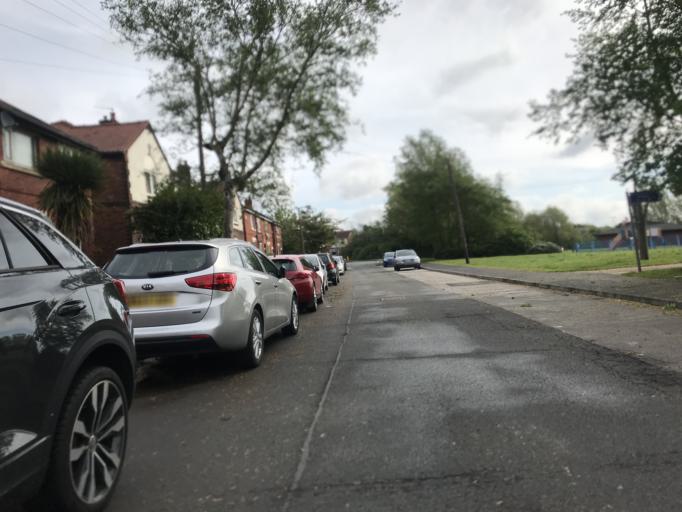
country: GB
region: England
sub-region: Borough of Stockport
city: Cheadle Heath
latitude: 53.4091
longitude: -2.1876
